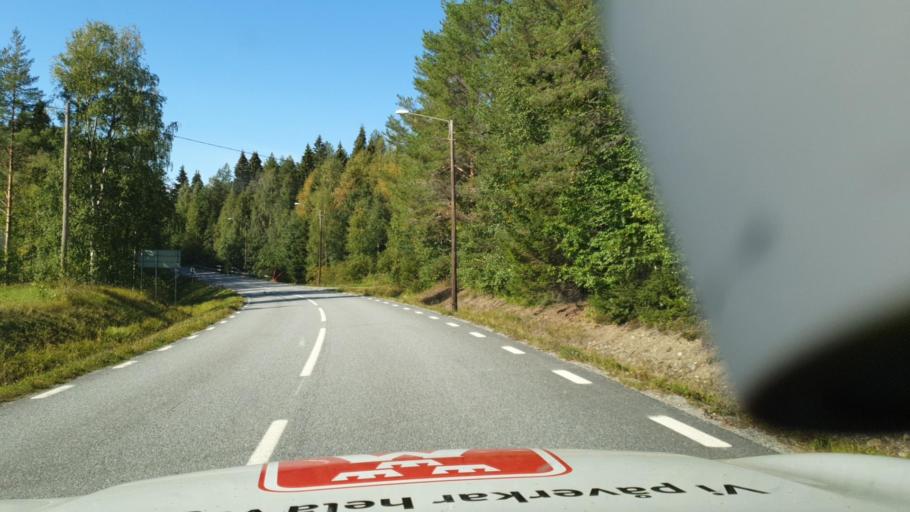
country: SE
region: Vaesterbotten
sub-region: Dorotea Kommun
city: Dorotea
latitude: 64.1176
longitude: 16.2225
